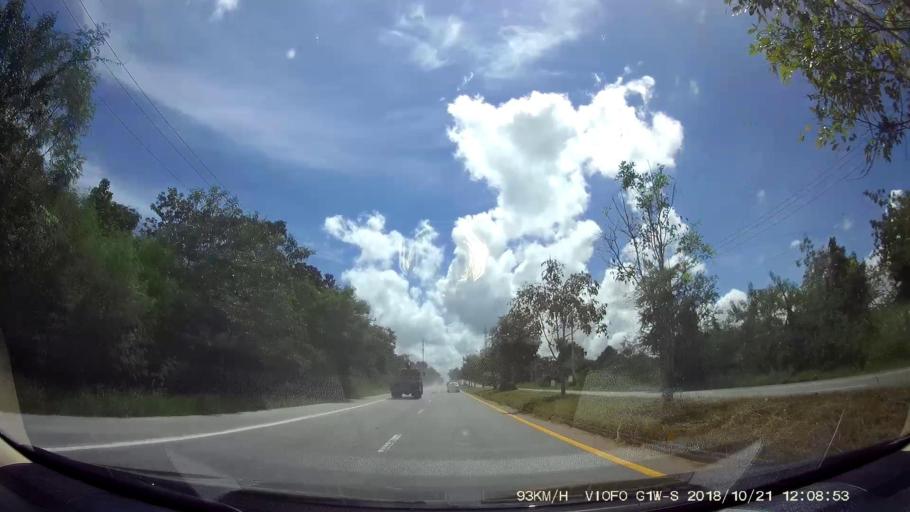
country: TH
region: Chaiyaphum
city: Chatturat
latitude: 15.4278
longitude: 101.8315
